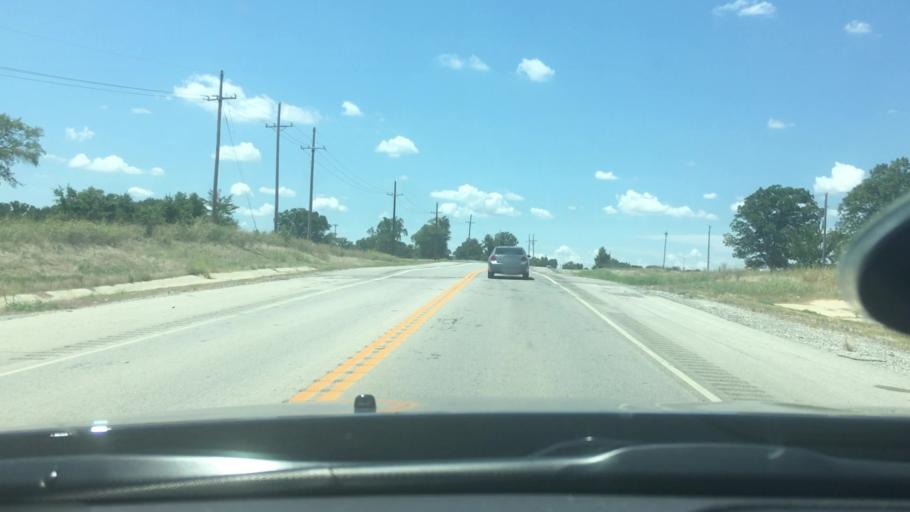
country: US
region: Oklahoma
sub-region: Bryan County
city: Durant
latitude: 33.9977
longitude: -96.2440
